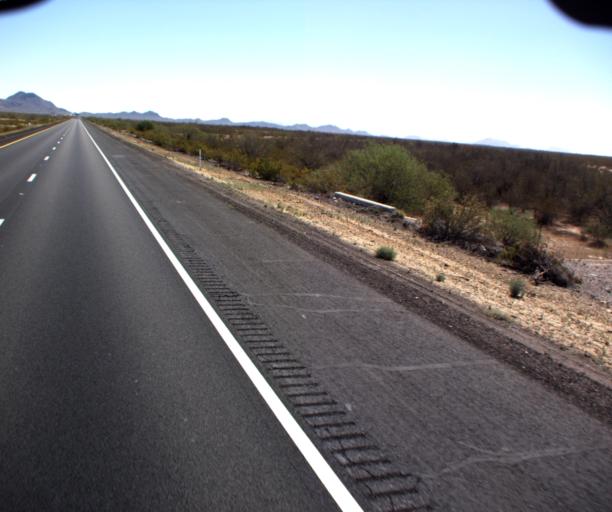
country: US
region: Arizona
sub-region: La Paz County
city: Salome
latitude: 33.6232
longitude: -113.7167
